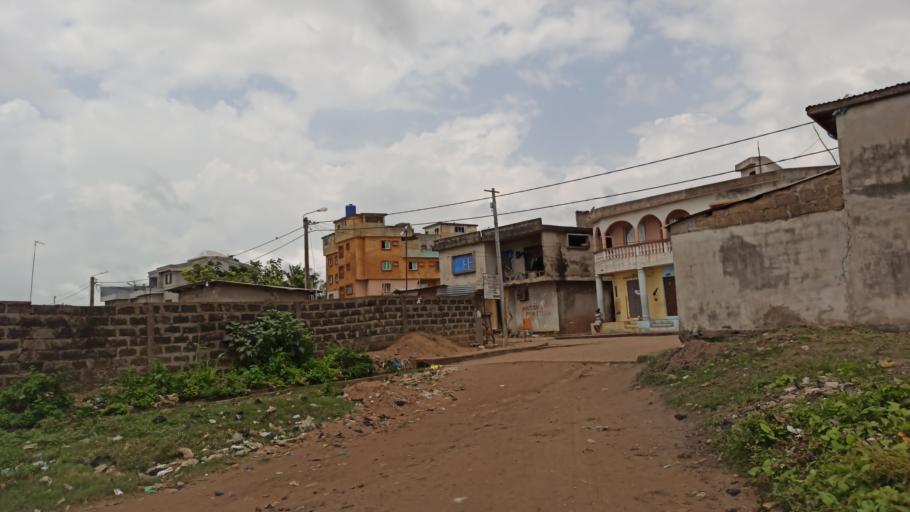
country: BJ
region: Queme
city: Porto-Novo
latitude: 6.4686
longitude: 2.6314
